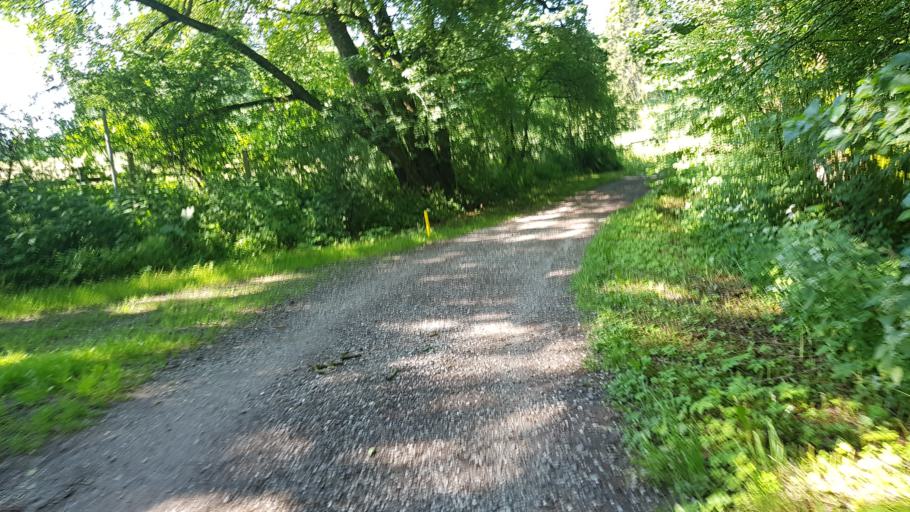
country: DE
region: Bavaria
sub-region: Upper Bavaria
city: Starnberg
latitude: 48.0083
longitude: 11.3703
